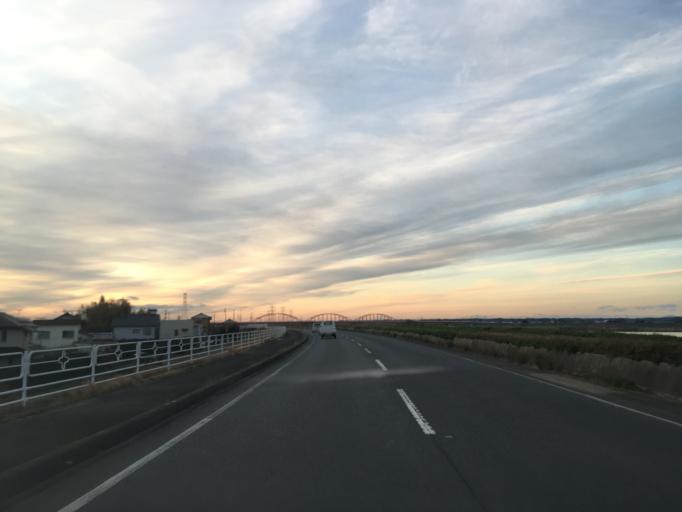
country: JP
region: Chiba
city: Katori-shi
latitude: 35.9069
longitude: 140.4053
